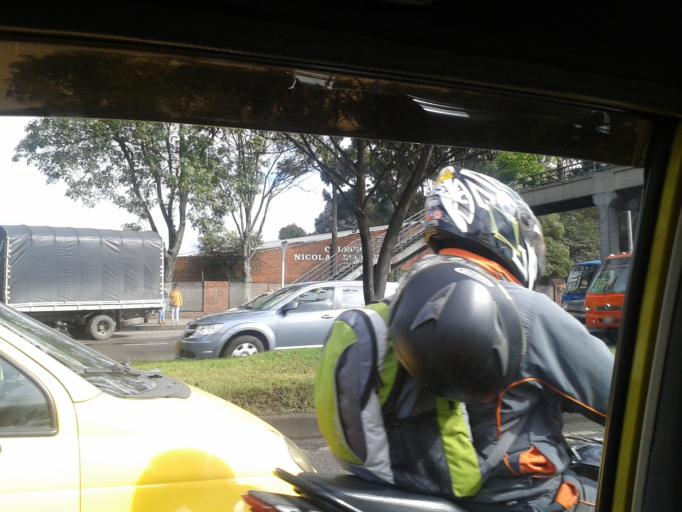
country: CO
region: Bogota D.C.
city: Bogota
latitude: 4.6325
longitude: -74.1210
